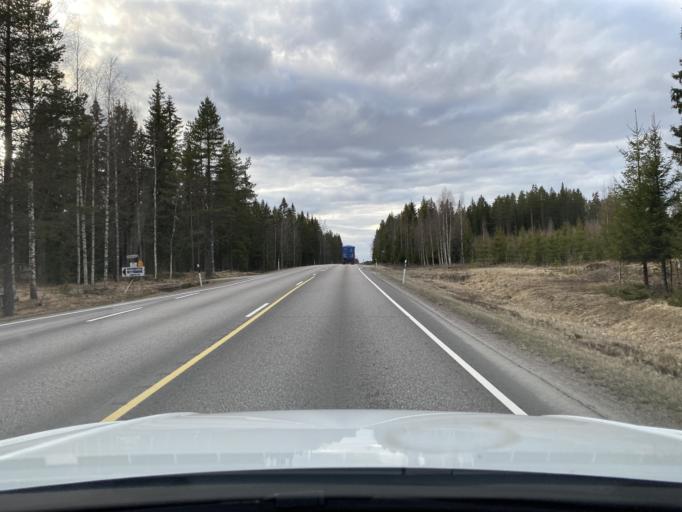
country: FI
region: Uusimaa
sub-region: Helsinki
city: Kaerkoelae
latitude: 60.8044
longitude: 24.0730
